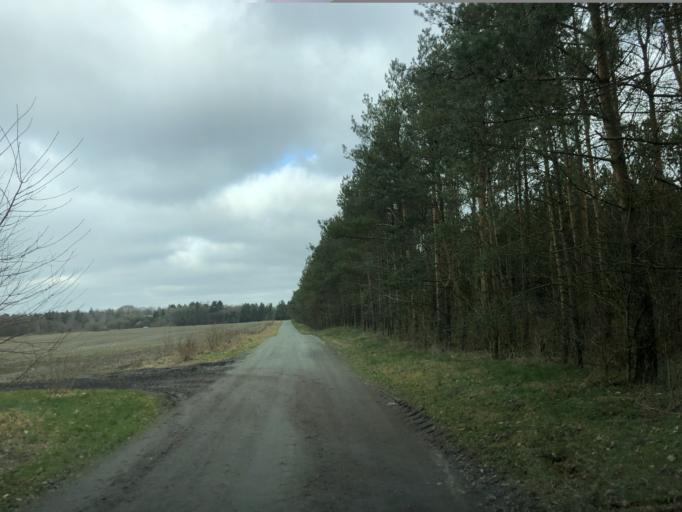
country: DK
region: South Denmark
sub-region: Billund Kommune
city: Billund
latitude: 55.7741
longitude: 9.1382
